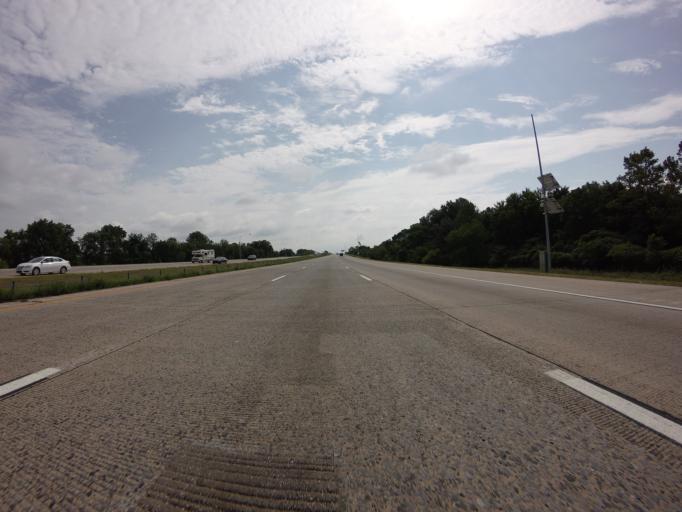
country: US
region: Delaware
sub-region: New Castle County
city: Wilmington
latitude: 39.7169
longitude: -75.5645
